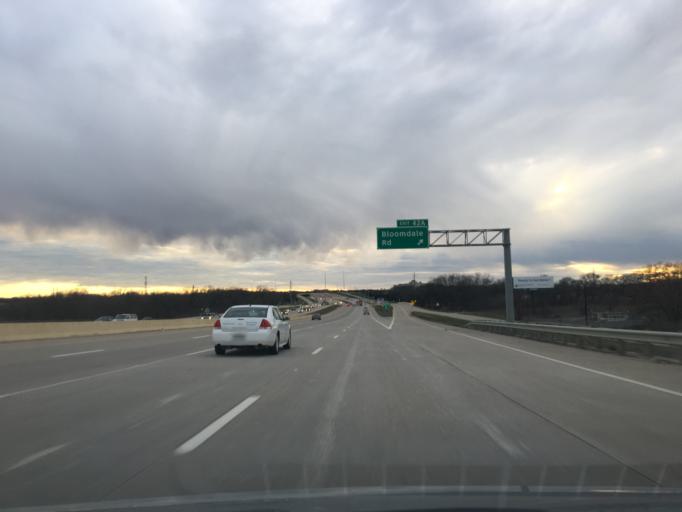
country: US
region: Texas
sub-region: Collin County
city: McKinney
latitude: 33.2493
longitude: -96.6201
